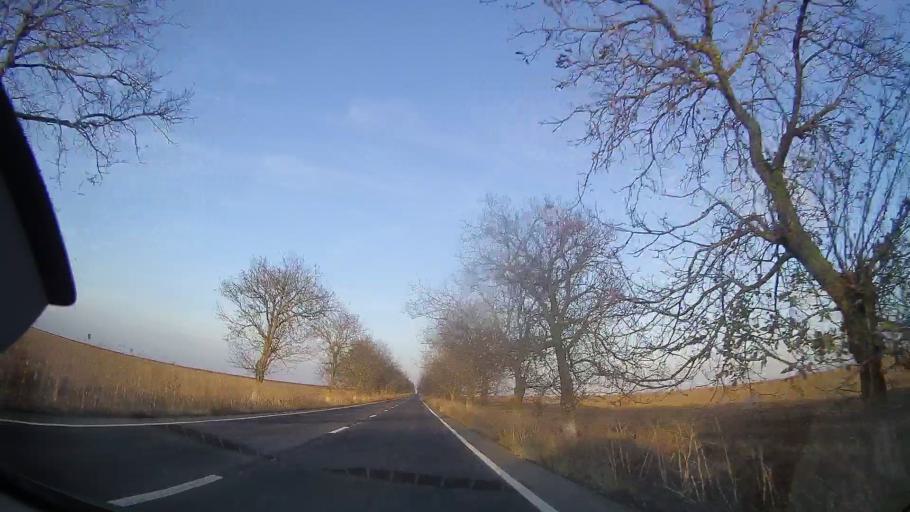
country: RO
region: Constanta
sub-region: Comuna Comana
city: Comana
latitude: 43.9072
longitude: 28.3331
